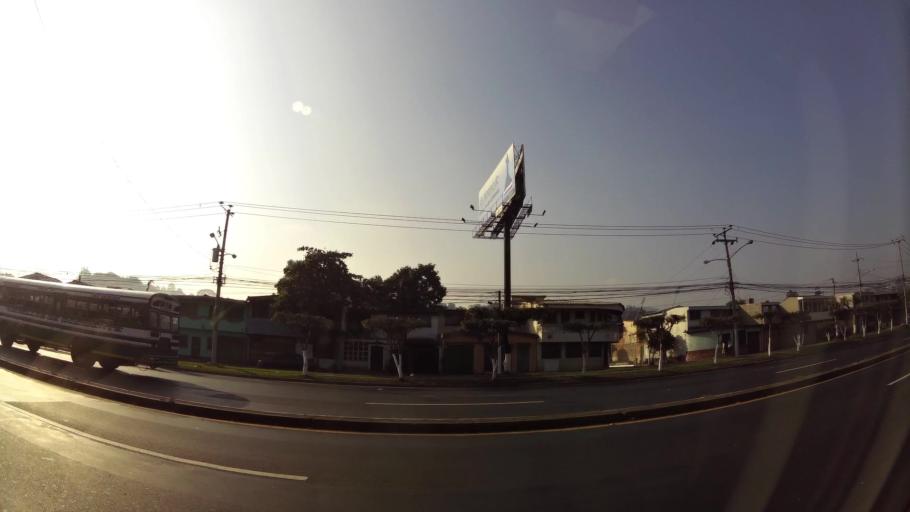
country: SV
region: San Salvador
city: San Salvador
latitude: 13.6845
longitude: -89.2204
